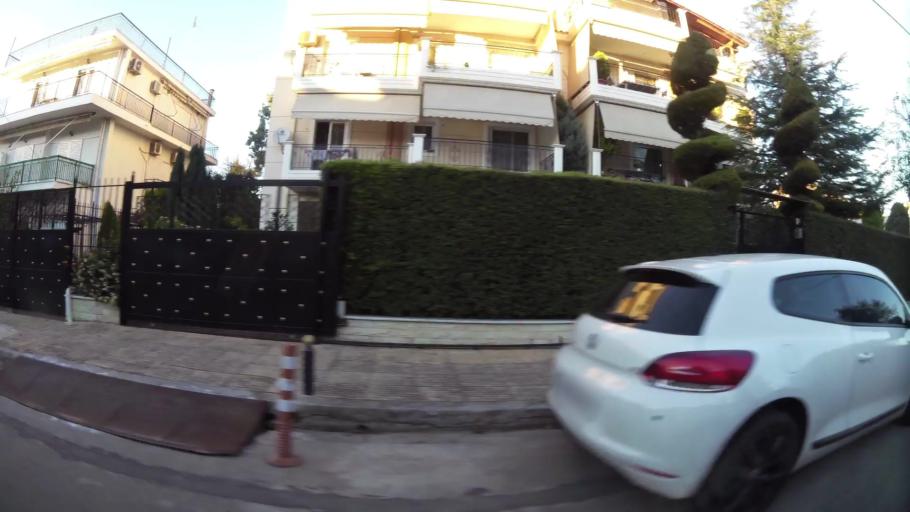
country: GR
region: Attica
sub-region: Nomarchia Athinas
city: Lykovrysi
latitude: 38.0675
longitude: 23.7883
